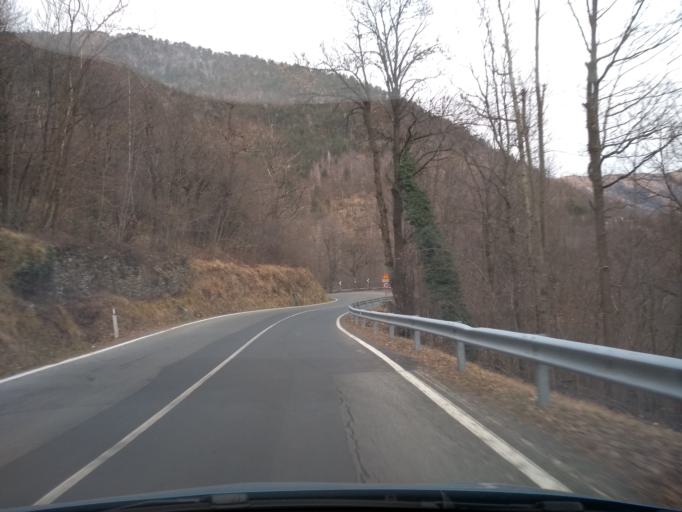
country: IT
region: Piedmont
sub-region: Provincia di Torino
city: Viu
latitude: 45.2376
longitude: 7.4087
